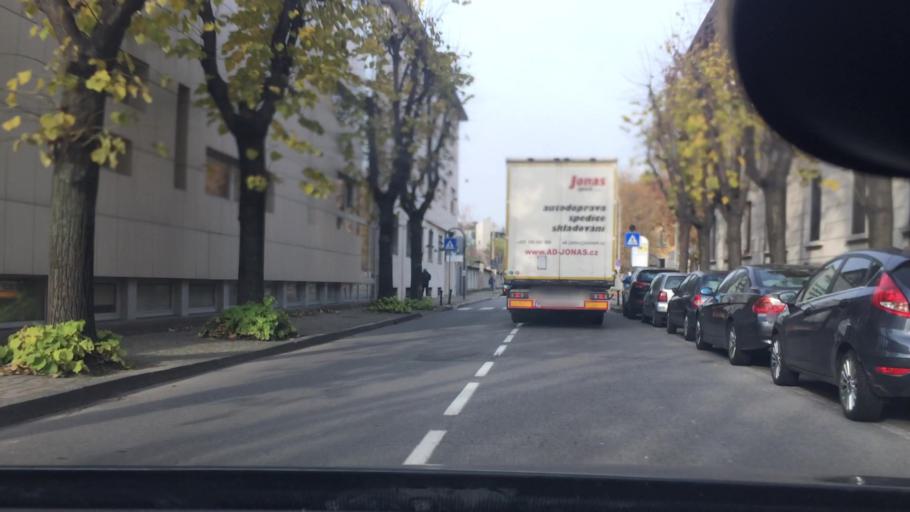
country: IT
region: Lombardy
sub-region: Citta metropolitana di Milano
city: Legnano
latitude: 45.5890
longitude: 8.9077
